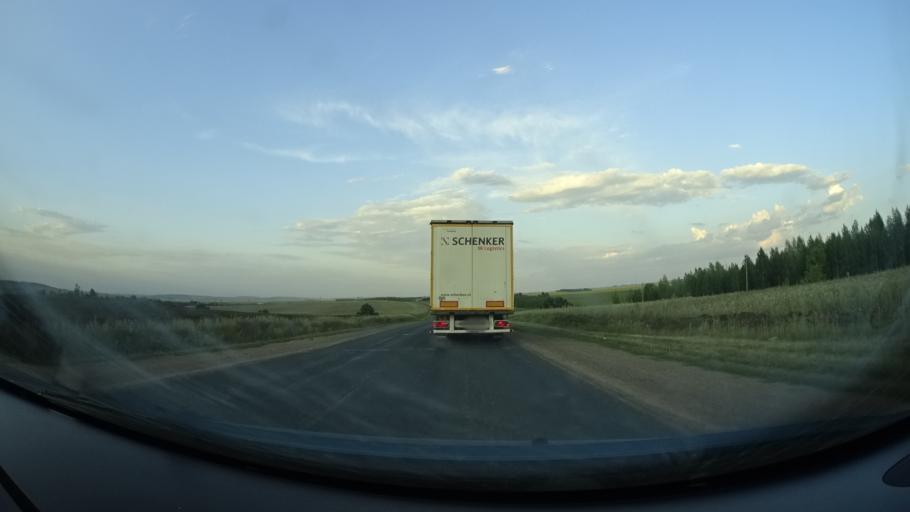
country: RU
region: Orenburg
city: Severnoye
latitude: 54.0871
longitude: 52.4379
